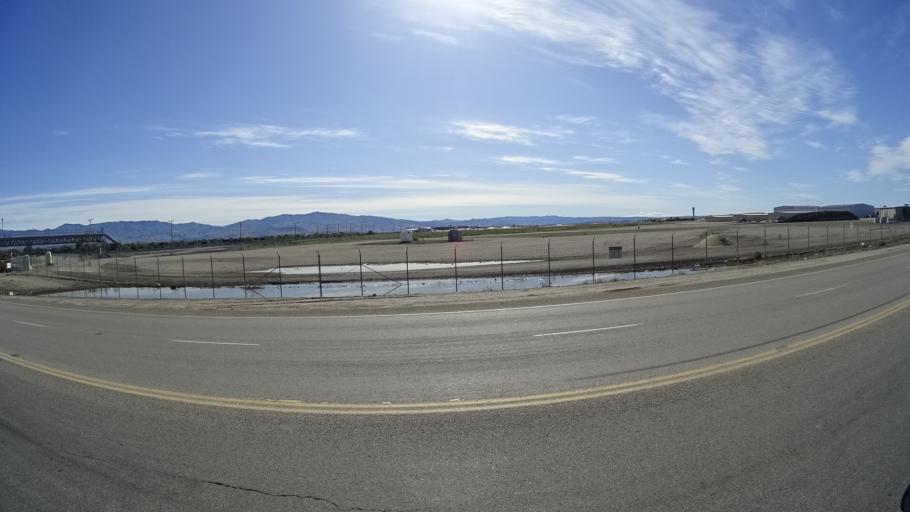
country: US
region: Idaho
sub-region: Ada County
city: Garden City
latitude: 43.5706
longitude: -116.2487
